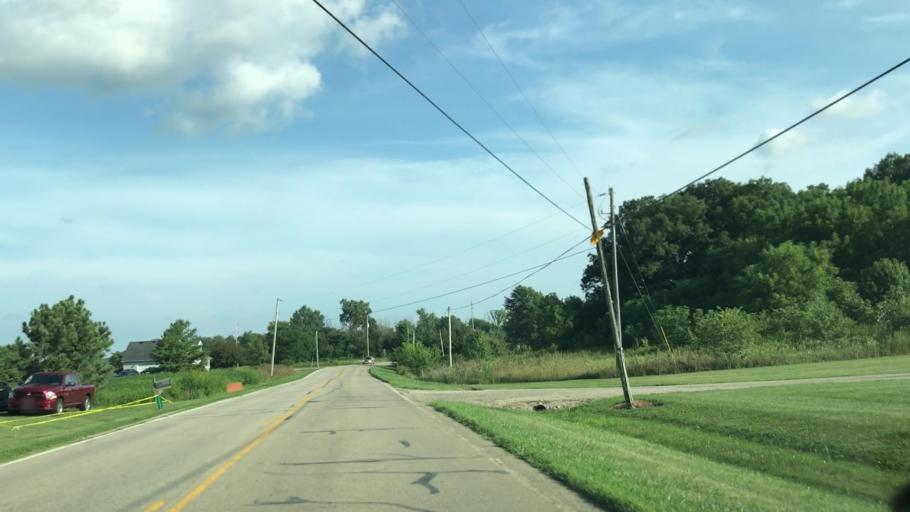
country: US
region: Ohio
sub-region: Union County
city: Marysville
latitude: 40.2166
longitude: -83.3556
